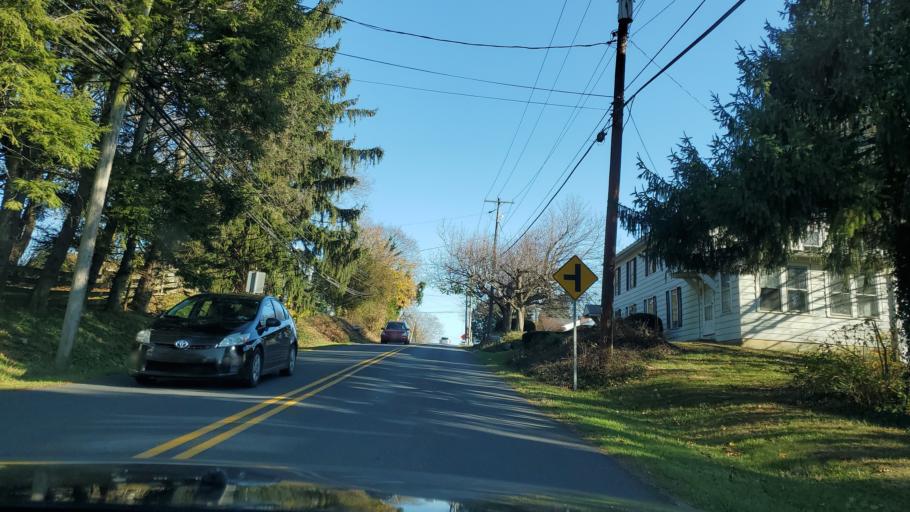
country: US
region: Pennsylvania
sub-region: Cumberland County
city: Mechanicsburg
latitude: 40.1769
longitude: -76.9919
